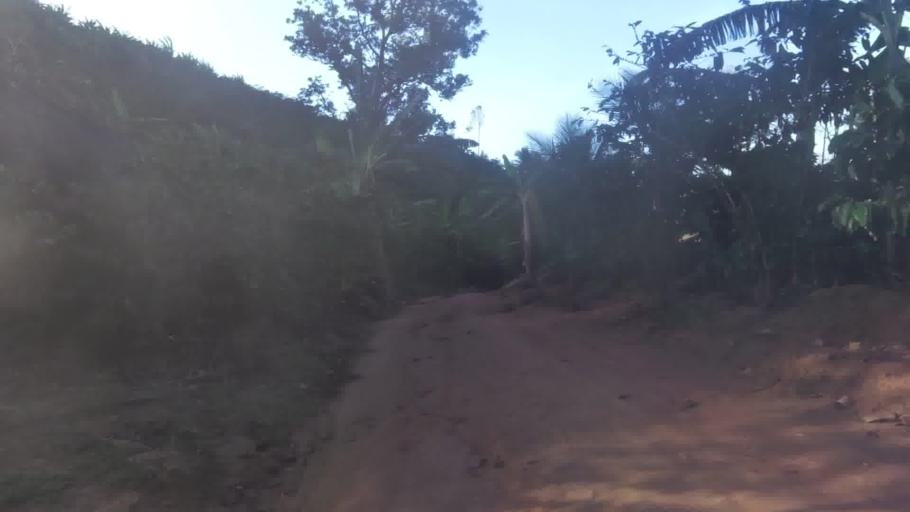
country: BR
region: Espirito Santo
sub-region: Iconha
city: Iconha
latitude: -20.7529
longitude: -40.8082
